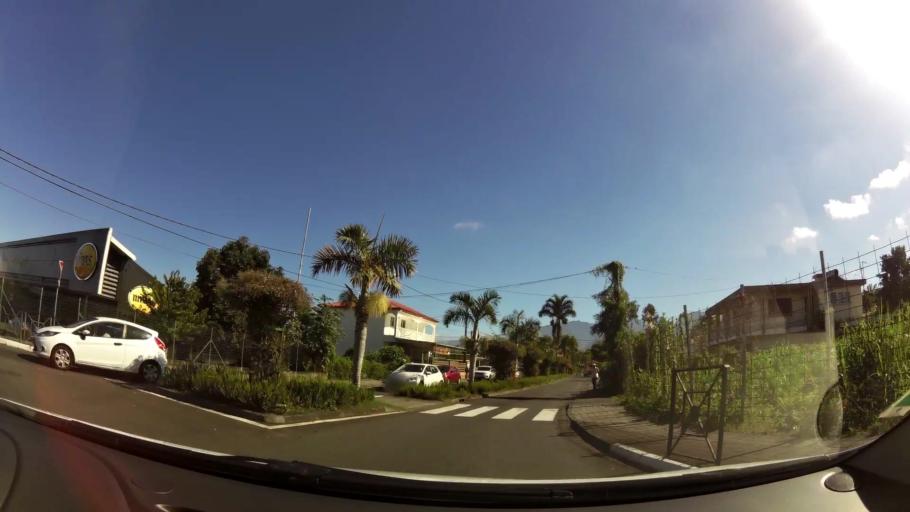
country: RE
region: Reunion
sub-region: Reunion
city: Le Tampon
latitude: -21.2719
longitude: 55.5158
